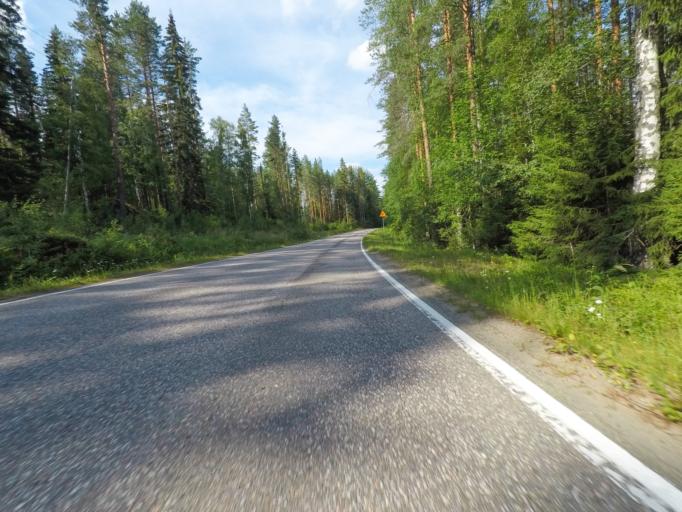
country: FI
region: Southern Savonia
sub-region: Savonlinna
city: Sulkava
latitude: 61.7681
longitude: 28.2354
